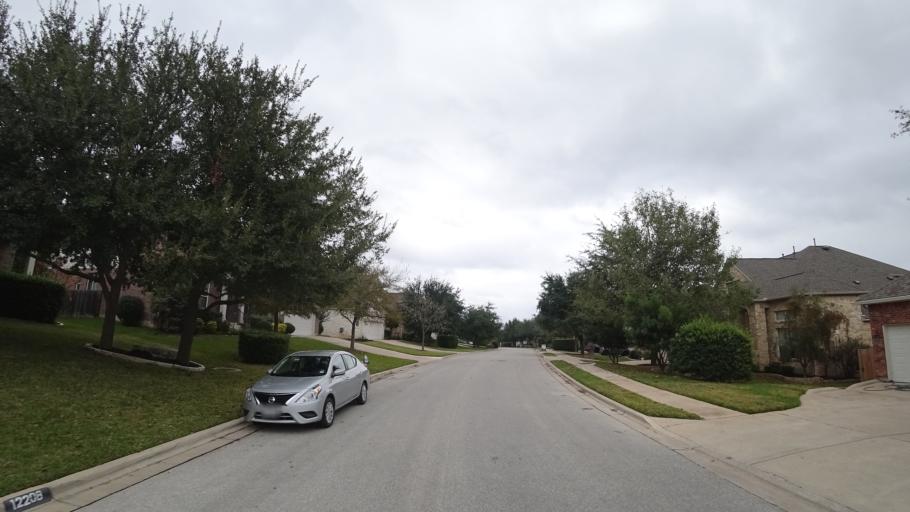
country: US
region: Texas
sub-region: Travis County
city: Hudson Bend
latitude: 30.3597
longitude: -97.8993
